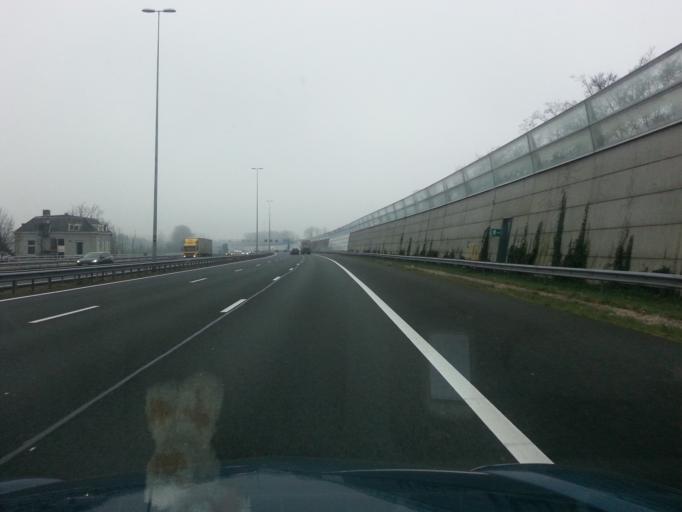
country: NL
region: Gelderland
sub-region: Gemeente Rozendaal
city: Rozendaal
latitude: 51.9955
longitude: 5.9524
